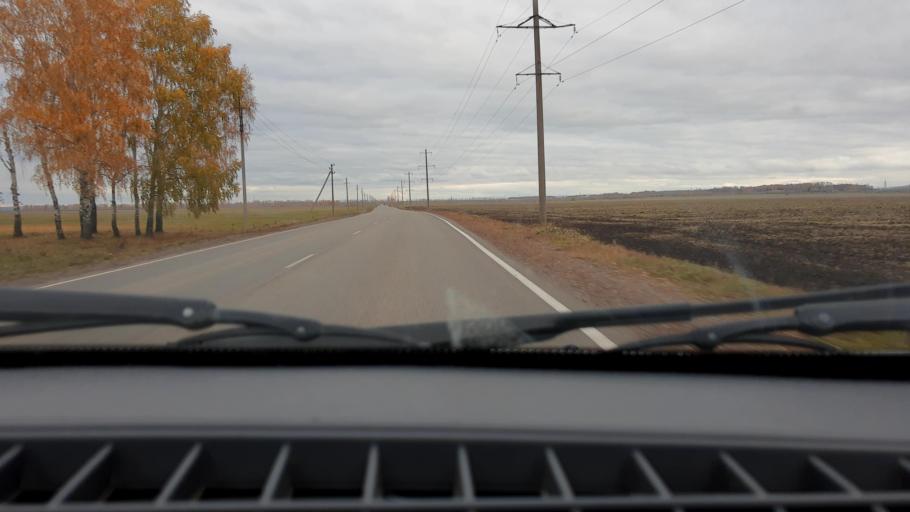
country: RU
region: Bashkortostan
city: Kabakovo
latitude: 54.5445
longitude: 56.0459
